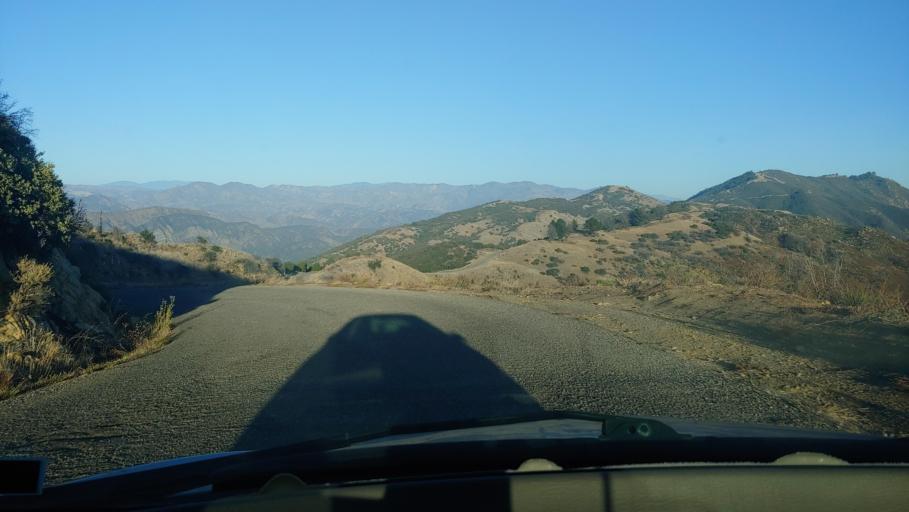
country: US
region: California
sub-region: Santa Barbara County
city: Mission Canyon
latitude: 34.5059
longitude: -119.7671
